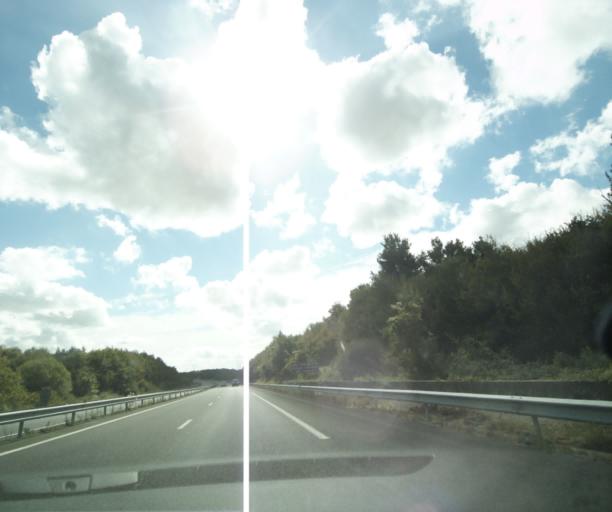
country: FR
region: Poitou-Charentes
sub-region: Departement de la Charente-Maritime
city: Saint-Georges-des-Coteaux
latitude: 45.8089
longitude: -0.6958
